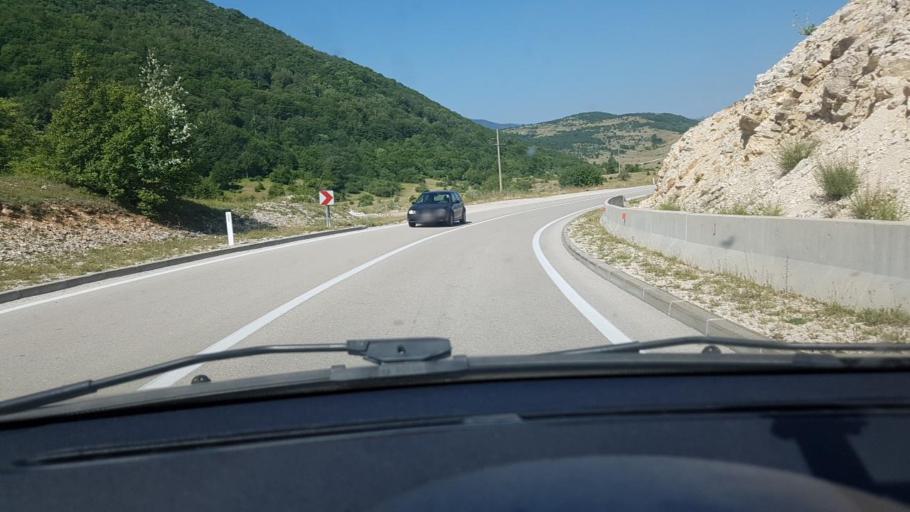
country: BA
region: Federation of Bosnia and Herzegovina
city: Bosansko Grahovo
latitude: 44.1289
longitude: 16.4980
